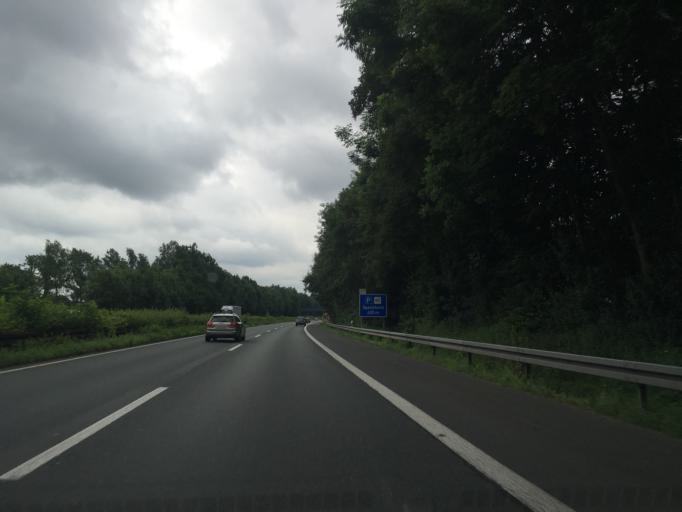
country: DE
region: North Rhine-Westphalia
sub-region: Regierungsbezirk Munster
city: Recklinghausen
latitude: 51.6467
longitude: 7.1718
